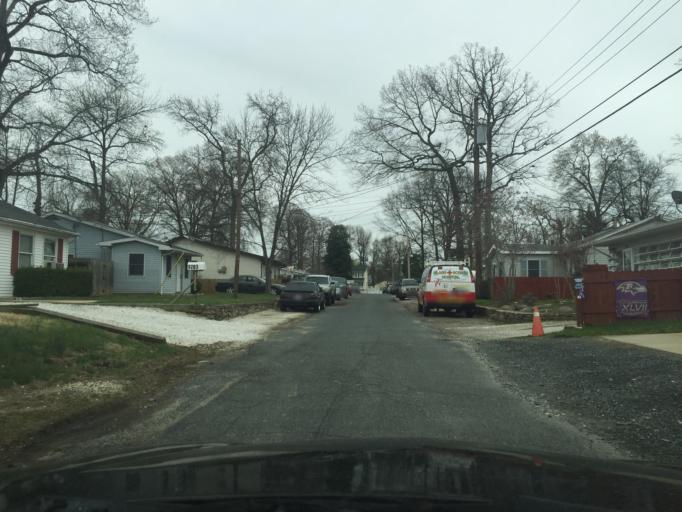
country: US
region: Maryland
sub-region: Baltimore County
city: Middle River
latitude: 39.3195
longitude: -76.4228
